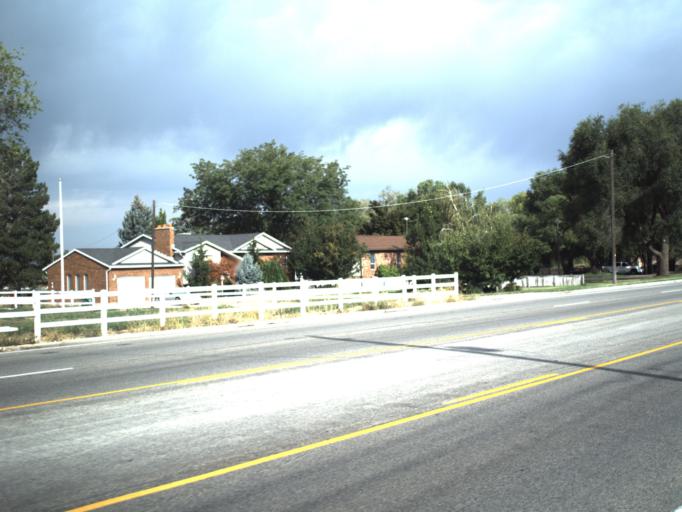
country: US
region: Utah
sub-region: Weber County
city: Harrisville
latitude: 41.2706
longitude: -111.9693
